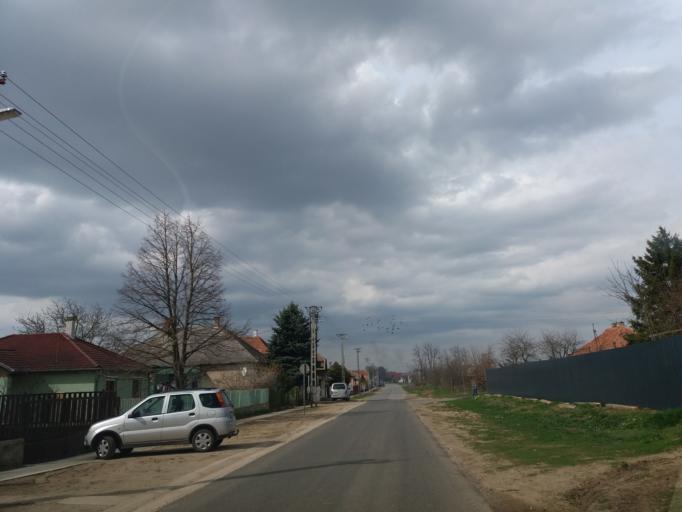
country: HU
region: Szabolcs-Szatmar-Bereg
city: Nyirtass
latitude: 48.1024
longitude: 22.0281
